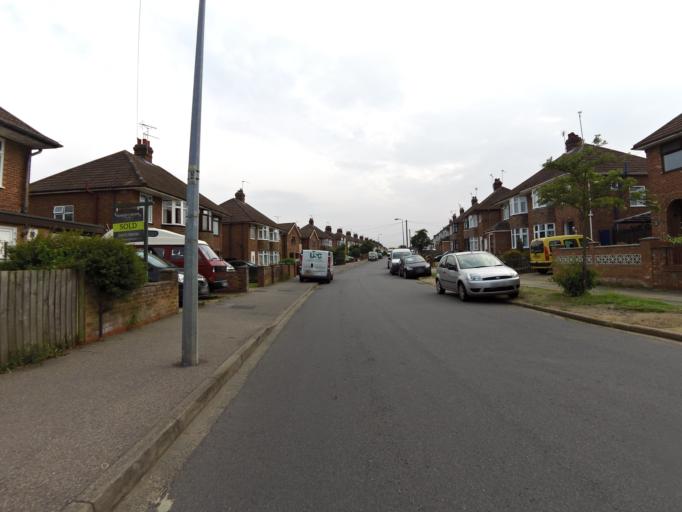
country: GB
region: England
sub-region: Suffolk
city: Ipswich
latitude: 52.0762
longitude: 1.1398
